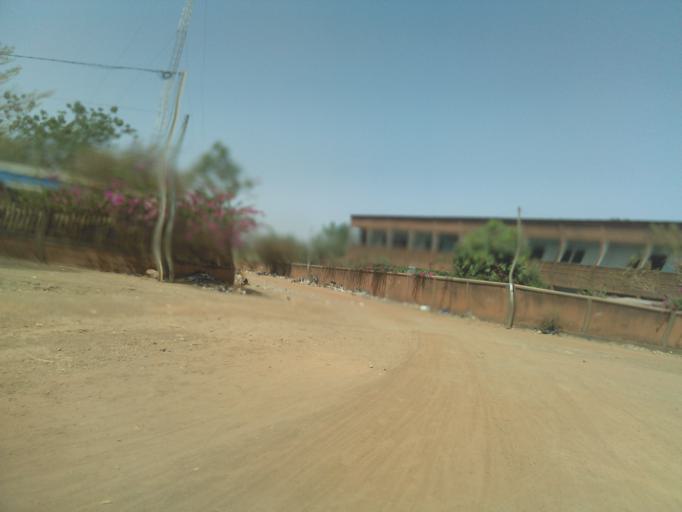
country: BF
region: Centre
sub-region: Kadiogo Province
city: Ouagadougou
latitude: 12.3935
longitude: -1.5679
